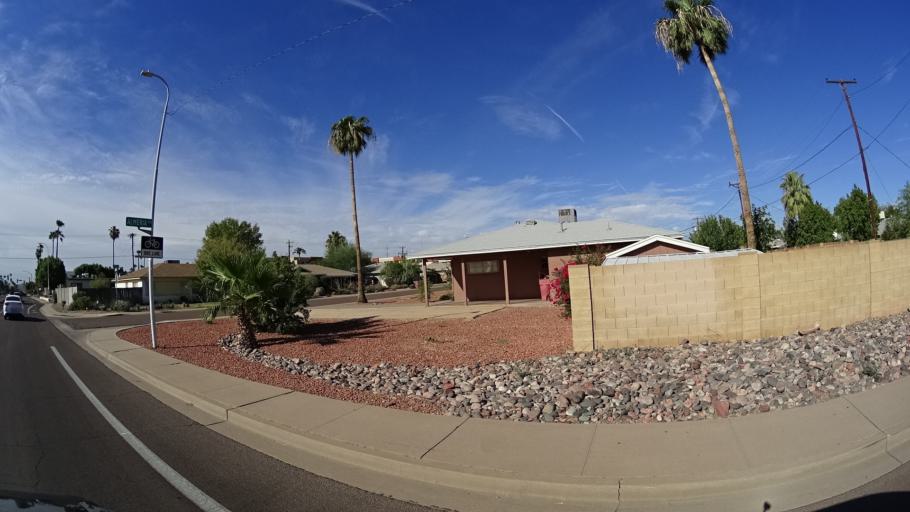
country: US
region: Arizona
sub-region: Maricopa County
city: Tempe Junction
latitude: 33.4672
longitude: -111.9349
